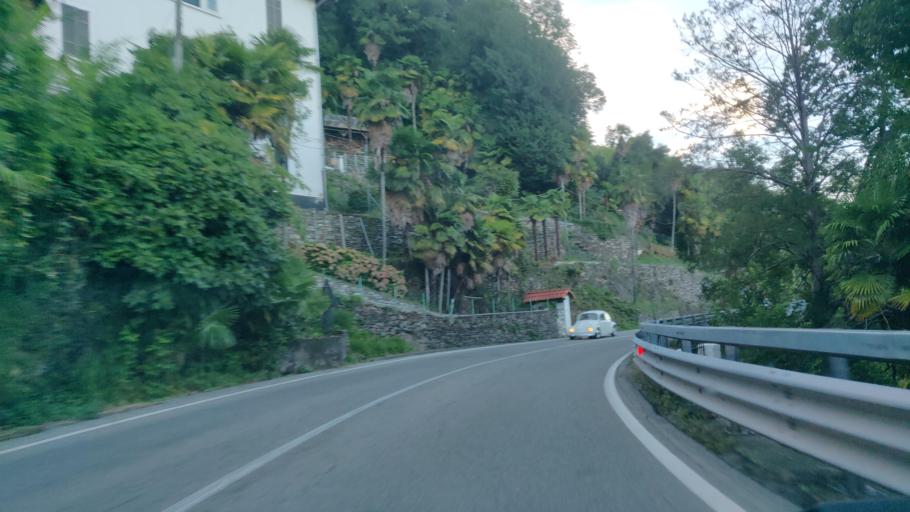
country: IT
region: Piedmont
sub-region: Provincia Verbano-Cusio-Ossola
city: Cannobio
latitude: 46.0472
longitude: 8.7048
